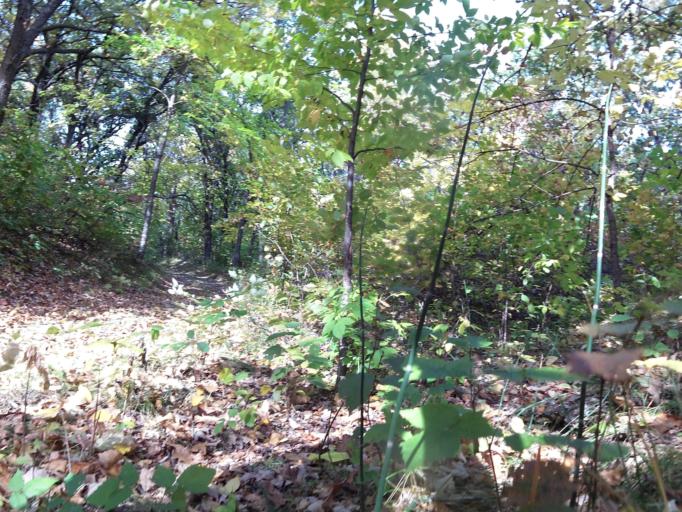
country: US
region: North Dakota
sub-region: Pembina County
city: Cavalier
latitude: 48.7794
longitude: -97.7319
